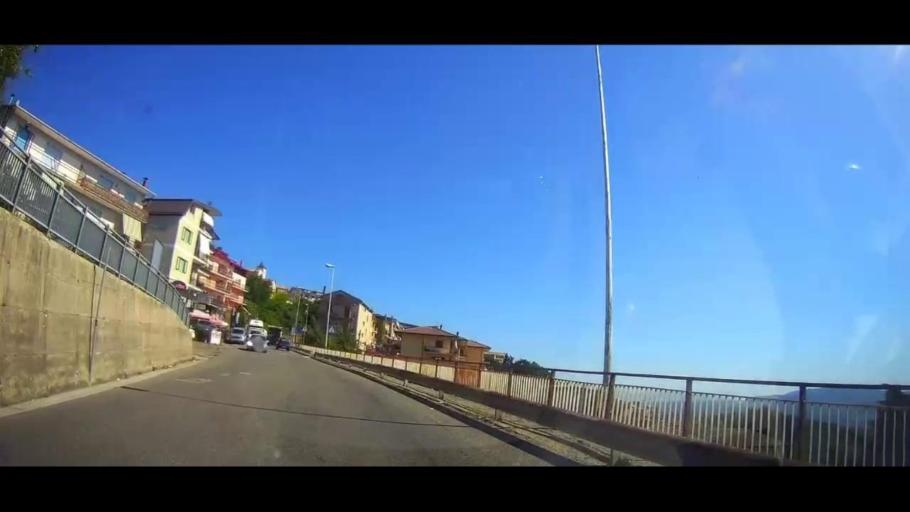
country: IT
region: Calabria
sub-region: Provincia di Cosenza
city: Celico
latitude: 39.3062
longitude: 16.3411
